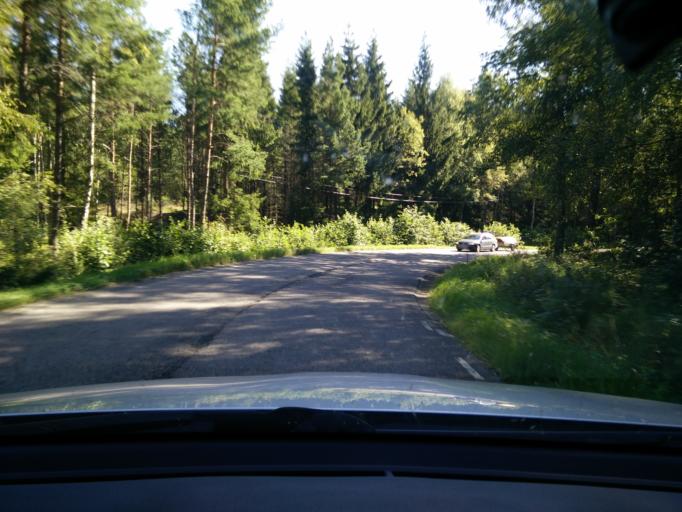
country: SE
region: Stockholm
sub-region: Lidingo
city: Lidingoe
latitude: 59.4677
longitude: 18.1763
